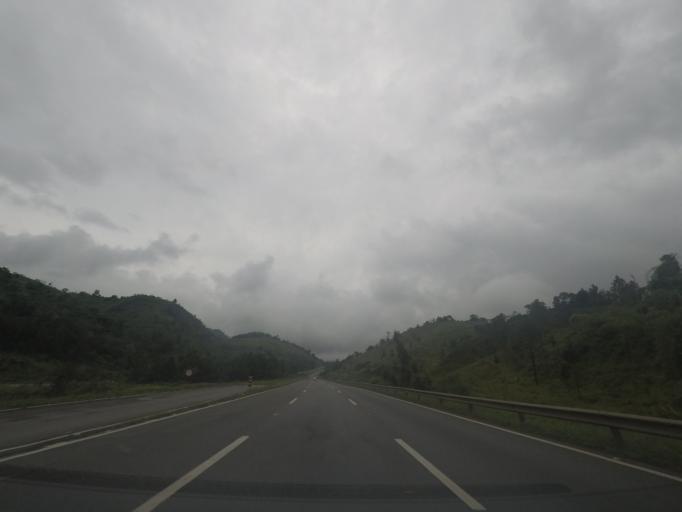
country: BR
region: Sao Paulo
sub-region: Cajati
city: Cajati
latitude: -24.9870
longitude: -48.5076
